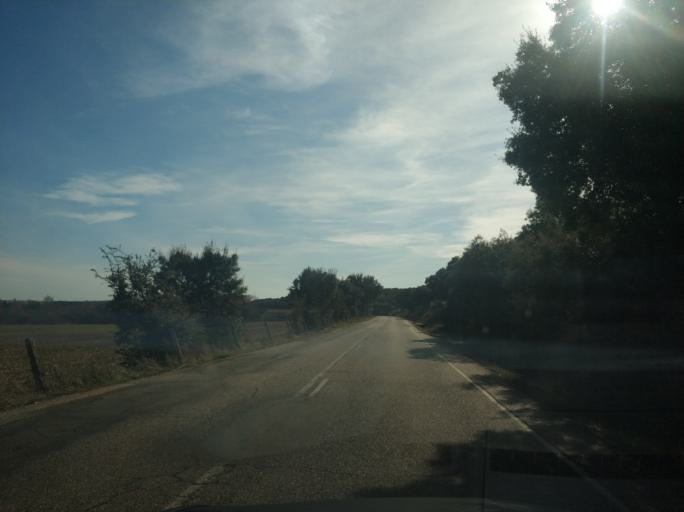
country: ES
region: Castille and Leon
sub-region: Provincia de Salamanca
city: Villamayor
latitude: 41.0025
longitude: -5.7324
